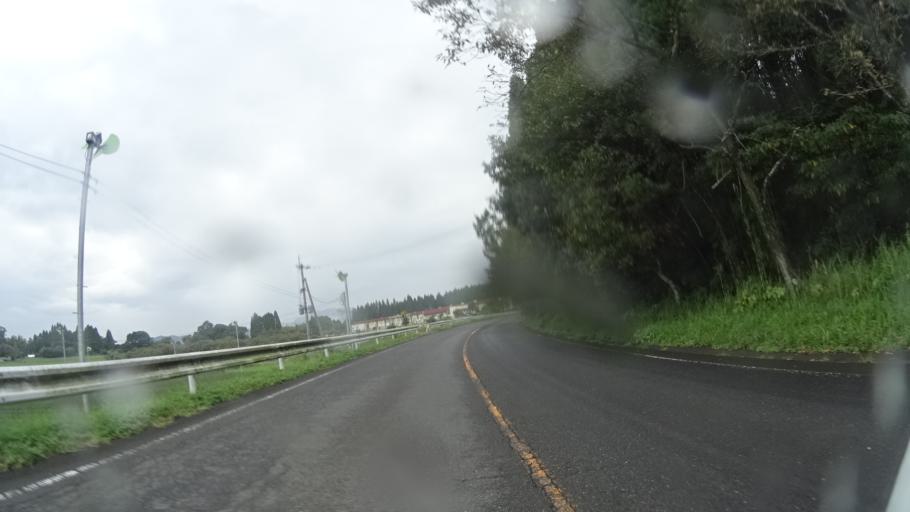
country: JP
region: Kagoshima
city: Kajiki
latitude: 31.7974
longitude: 130.6712
